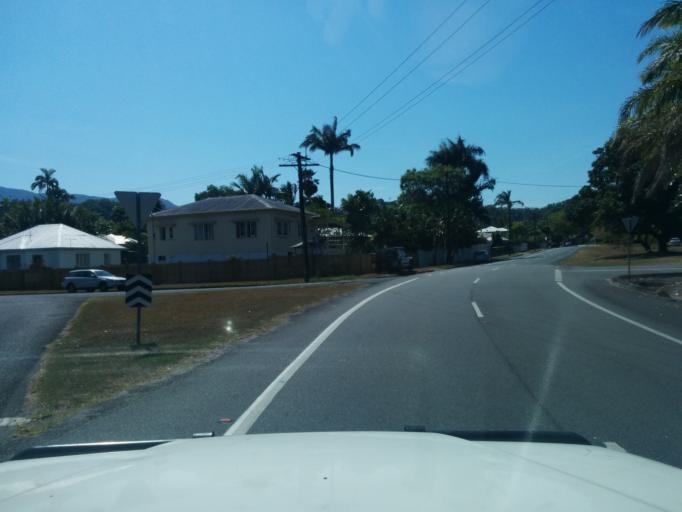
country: AU
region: Queensland
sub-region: Cairns
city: Redlynch
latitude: -16.9023
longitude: 145.7331
